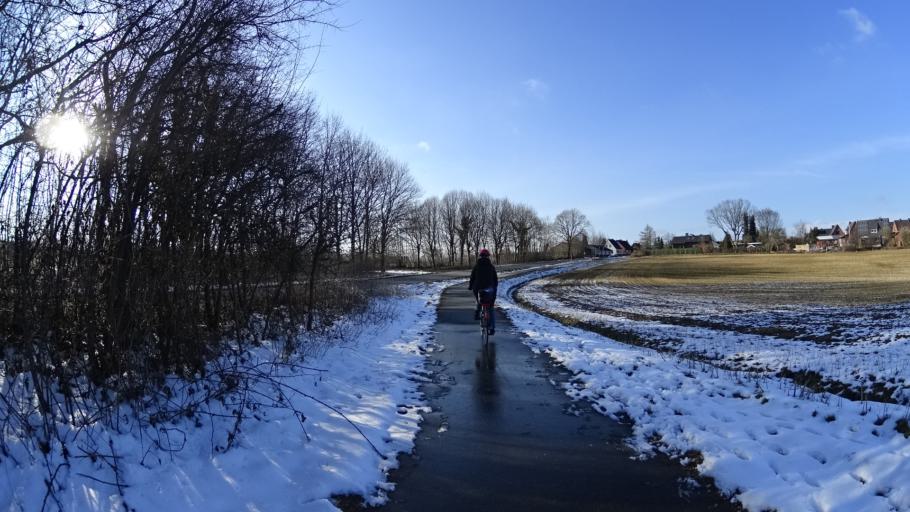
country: DE
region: Schleswig-Holstein
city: Martensrade
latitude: 54.2853
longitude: 10.3858
